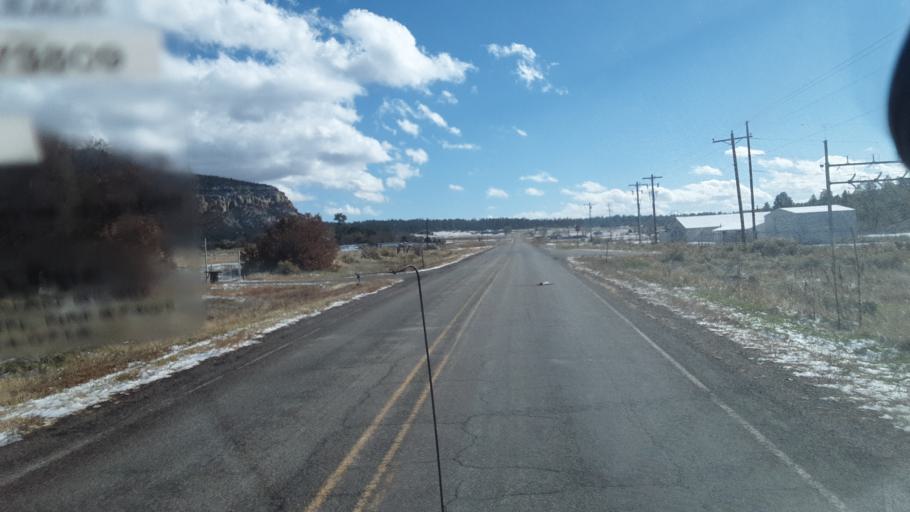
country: US
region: New Mexico
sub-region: Rio Arriba County
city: Santa Teresa
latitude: 36.2227
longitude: -106.7929
